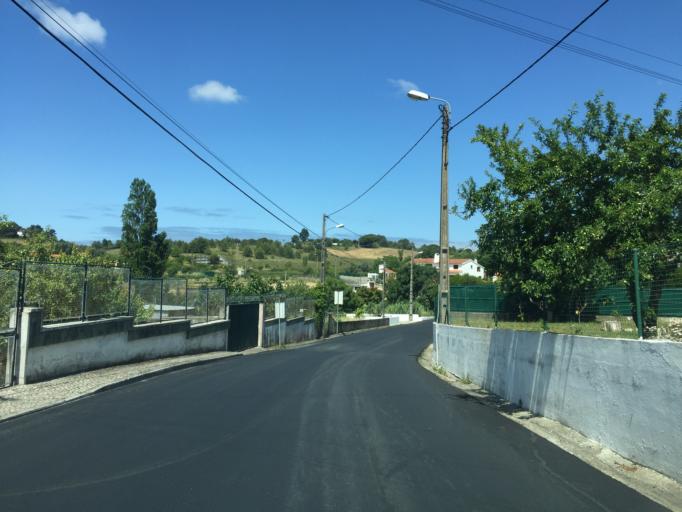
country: PT
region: Lisbon
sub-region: Sintra
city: Sintra
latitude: 38.8073
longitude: -9.4001
